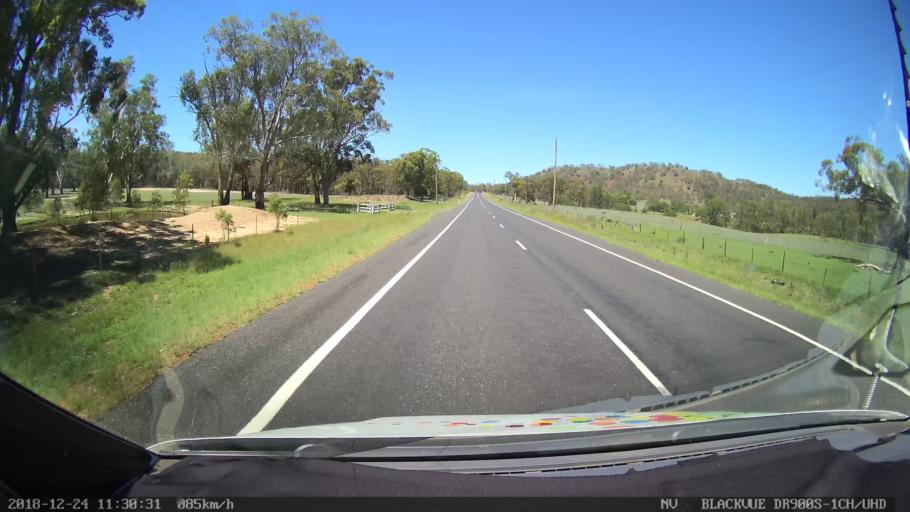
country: AU
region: New South Wales
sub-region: Upper Hunter Shire
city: Merriwa
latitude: -32.2056
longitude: 150.4657
